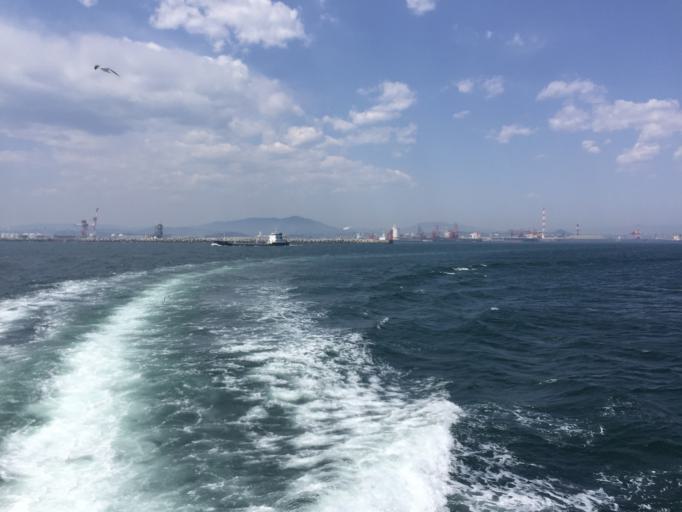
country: JP
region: Fukushima
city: Iwaki
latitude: 36.9149
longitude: 140.8881
